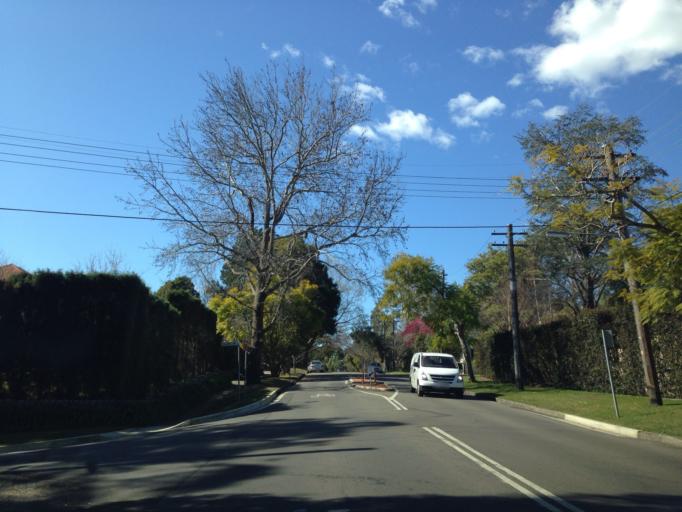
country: AU
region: New South Wales
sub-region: Ku-ring-gai
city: Killara
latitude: -33.7605
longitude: 151.1671
